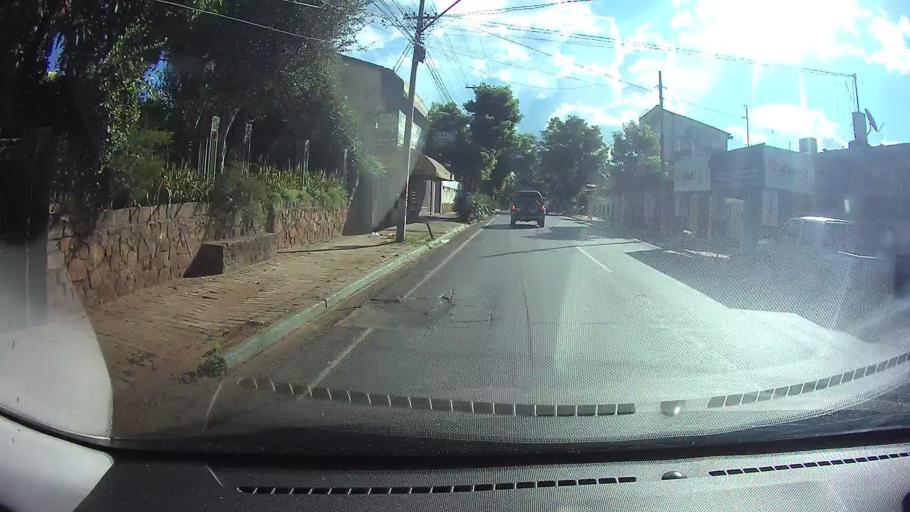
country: PY
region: Cordillera
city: Caacupe
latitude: -25.3832
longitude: -57.1382
